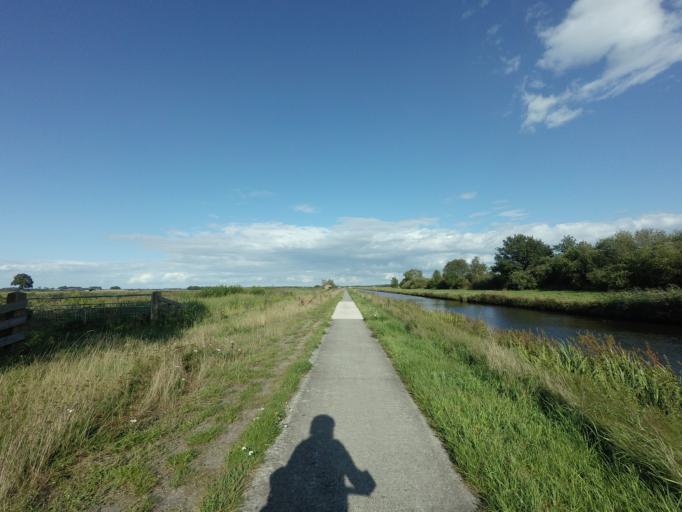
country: NL
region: Friesland
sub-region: Gemeente Heerenveen
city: Jubbega
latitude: 52.9844
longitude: 6.1883
